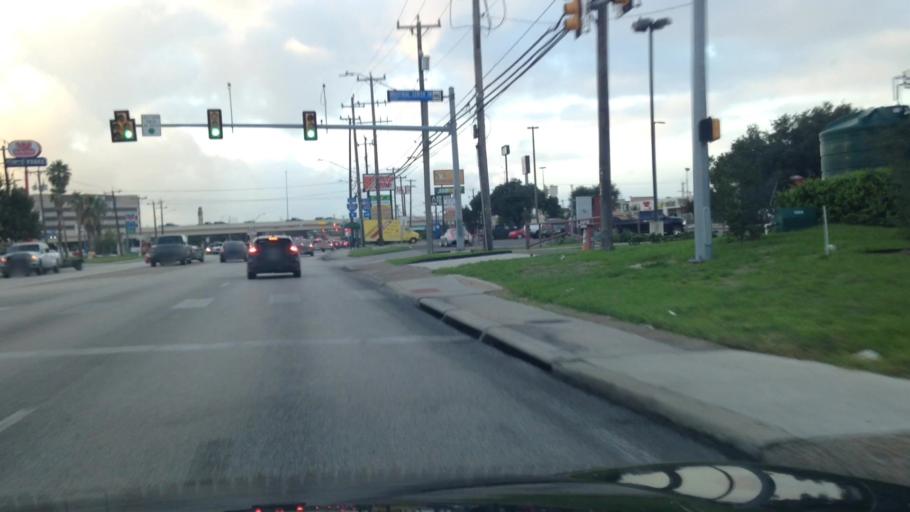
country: US
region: Texas
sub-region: Bexar County
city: Windcrest
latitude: 29.5186
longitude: -98.4111
